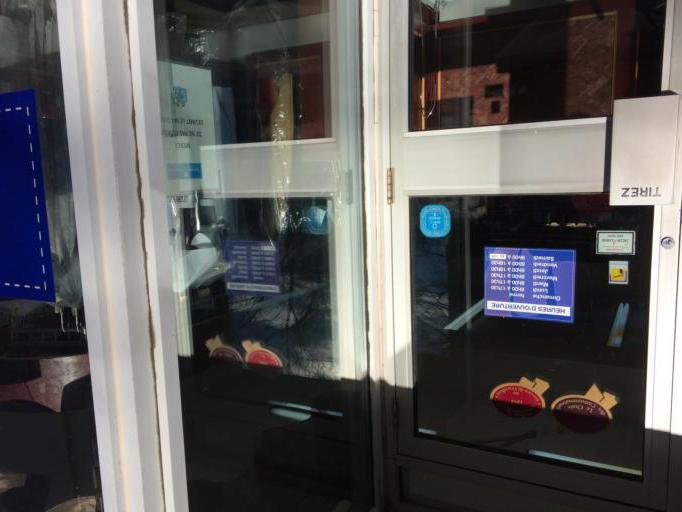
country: CA
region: Quebec
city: Quebec
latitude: 46.8036
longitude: -71.2295
